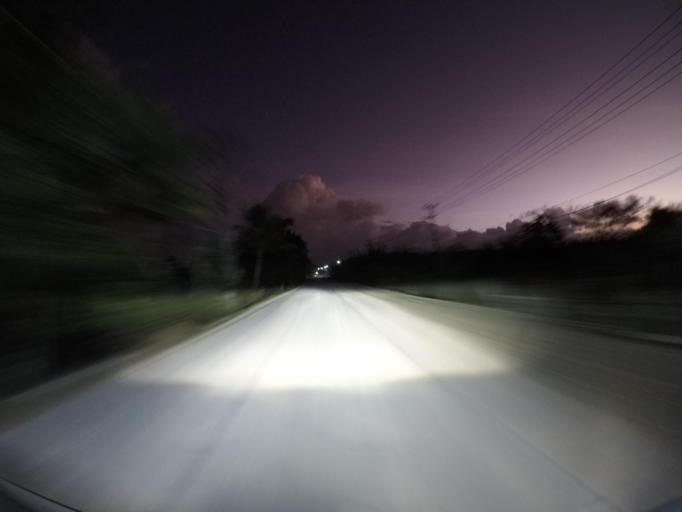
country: TL
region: Lautem
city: Lospalos
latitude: -8.4631
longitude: 126.9966
